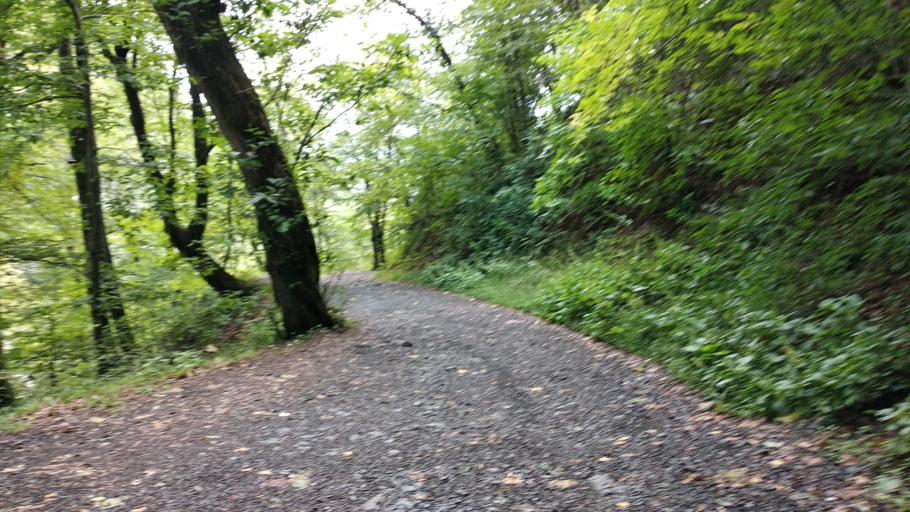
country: RU
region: Krasnodarskiy
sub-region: Sochi City
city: Sochi
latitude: 43.6360
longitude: 39.8149
